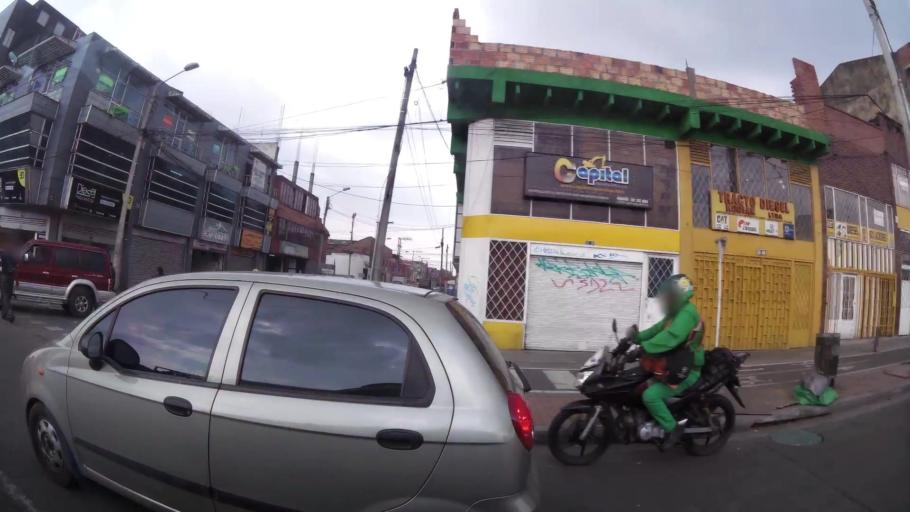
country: CO
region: Bogota D.C.
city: Bogota
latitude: 4.6034
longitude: -74.0936
